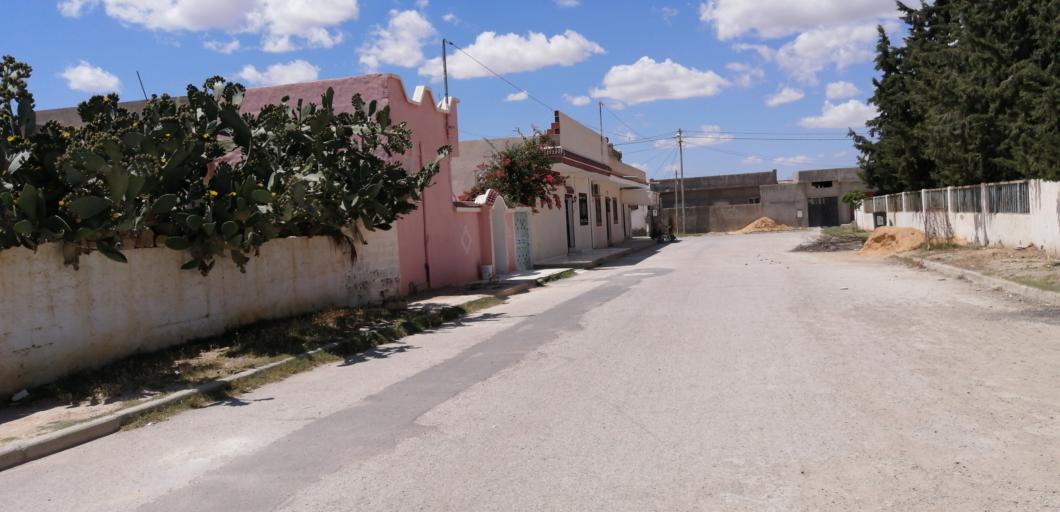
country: TN
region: Al Qayrawan
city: Kairouan
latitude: 35.6189
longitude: 9.9258
